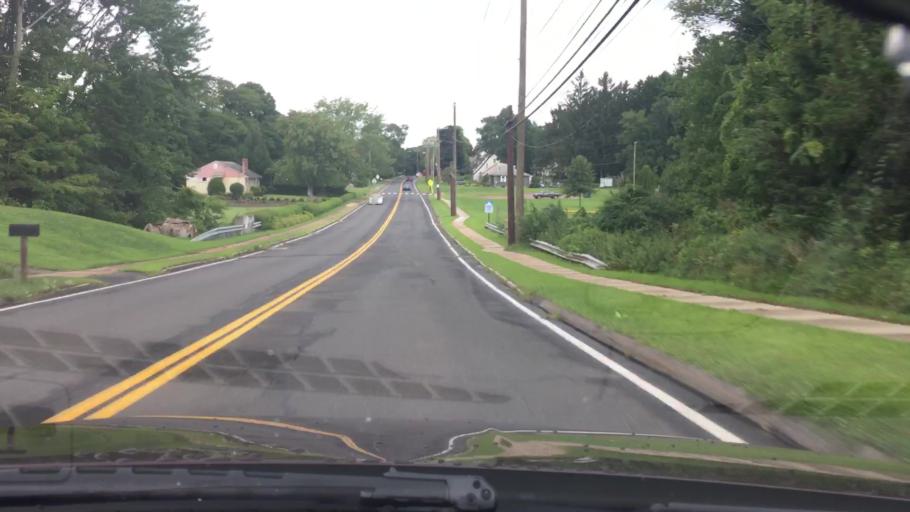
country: US
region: Connecticut
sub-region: Hartford County
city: Manchester
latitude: 41.7554
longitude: -72.5412
